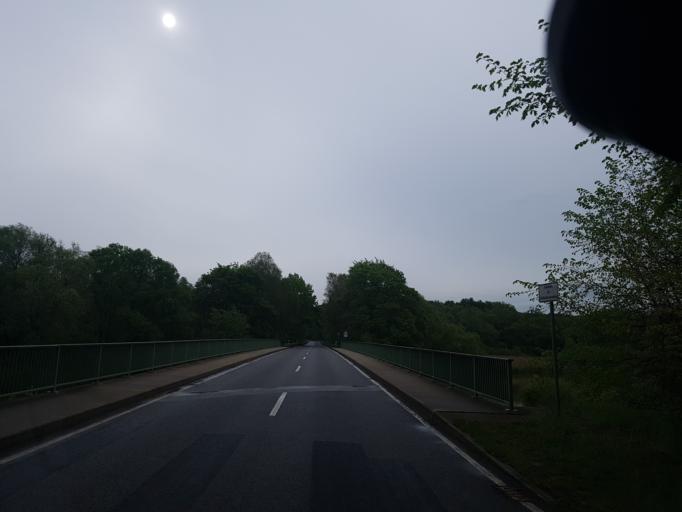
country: DE
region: Brandenburg
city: Spremberg
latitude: 51.6081
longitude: 14.3861
